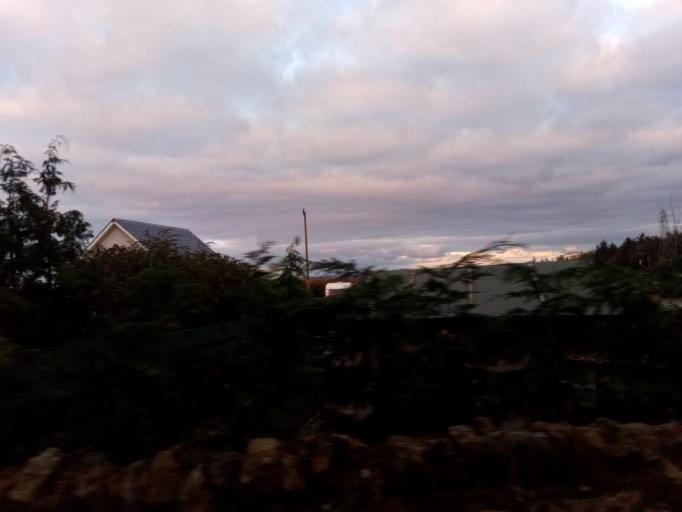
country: GB
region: Scotland
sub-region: Fife
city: Pathhead
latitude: 55.8760
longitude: -3.0043
